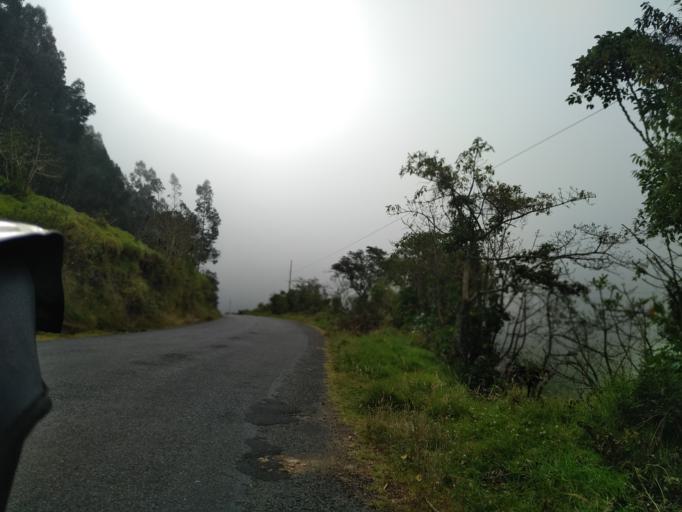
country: EC
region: Cotopaxi
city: Saquisili
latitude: -0.6956
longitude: -78.8139
